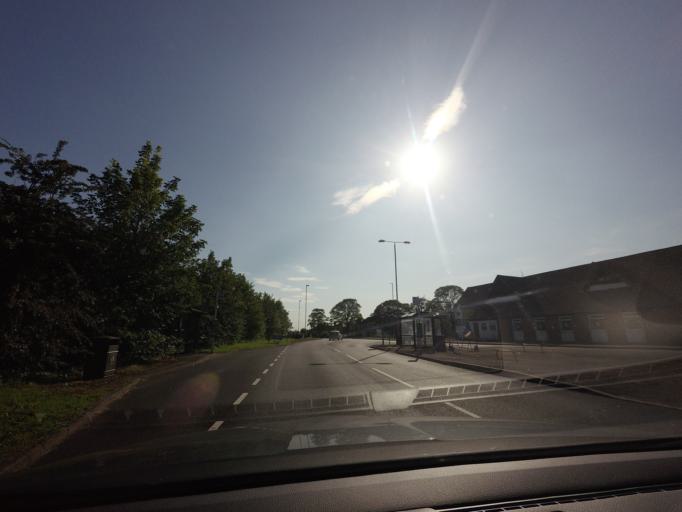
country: GB
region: England
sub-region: Derbyshire
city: Pinxton
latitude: 53.0507
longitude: -1.2934
